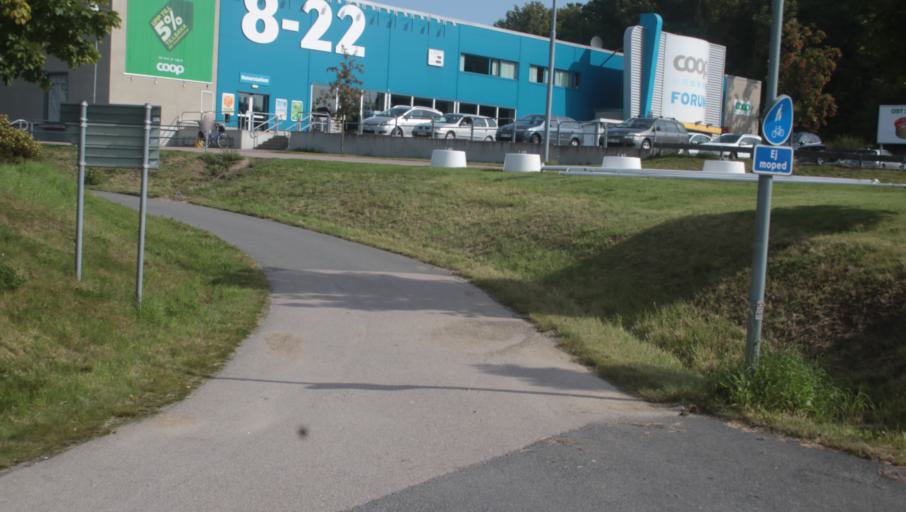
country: SE
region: Blekinge
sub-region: Karlshamns Kommun
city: Karlshamn
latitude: 56.1899
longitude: 14.8478
